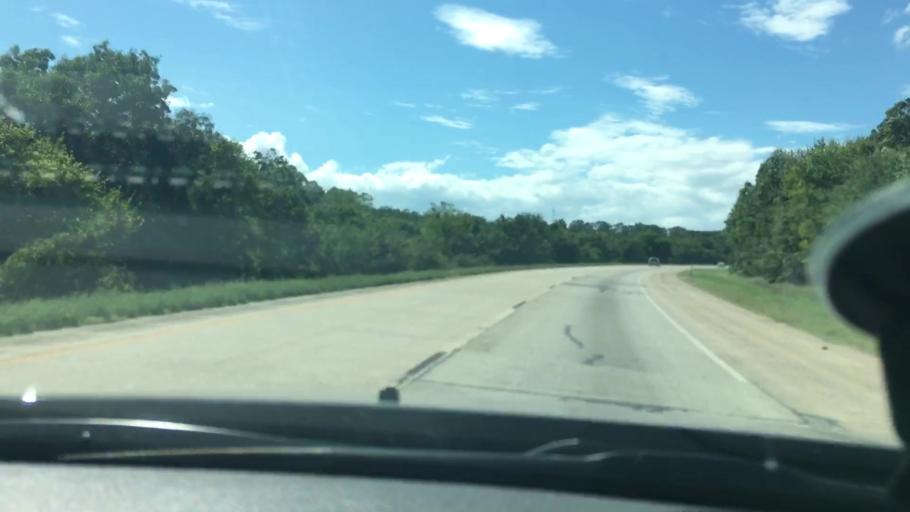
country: US
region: Oklahoma
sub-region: Sequoyah County
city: Vian
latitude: 35.4901
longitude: -94.9942
